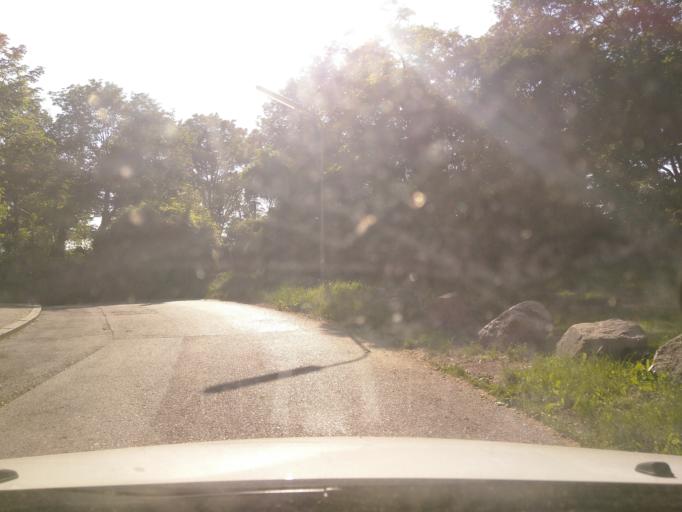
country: AT
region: Lower Austria
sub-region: Politischer Bezirk Modling
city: Perchtoldsdorf
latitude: 48.1799
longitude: 16.2890
